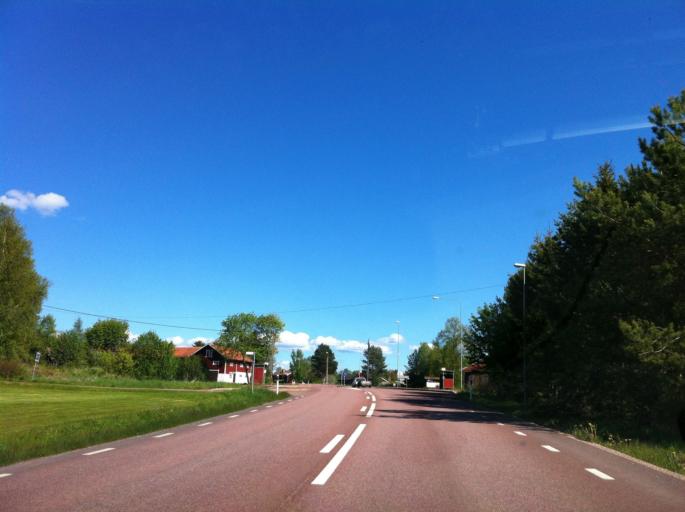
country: SE
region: Dalarna
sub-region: Leksand Municipality
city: Siljansnas
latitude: 60.9308
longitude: 14.7896
